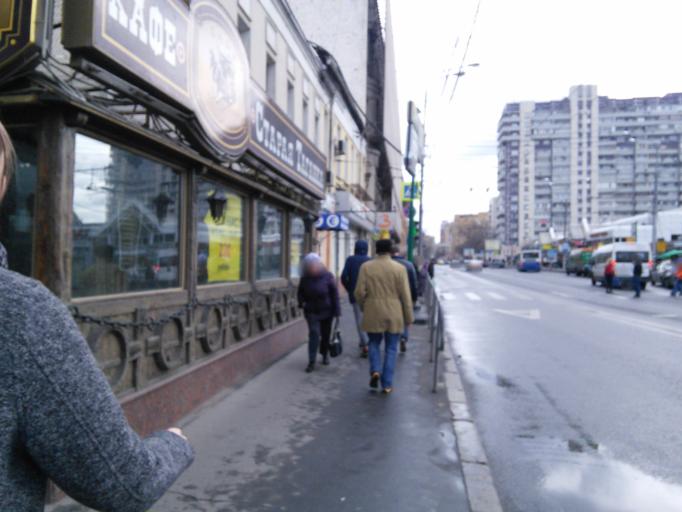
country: RU
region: Moscow
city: Taganskiy
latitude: 55.7415
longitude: 37.6563
